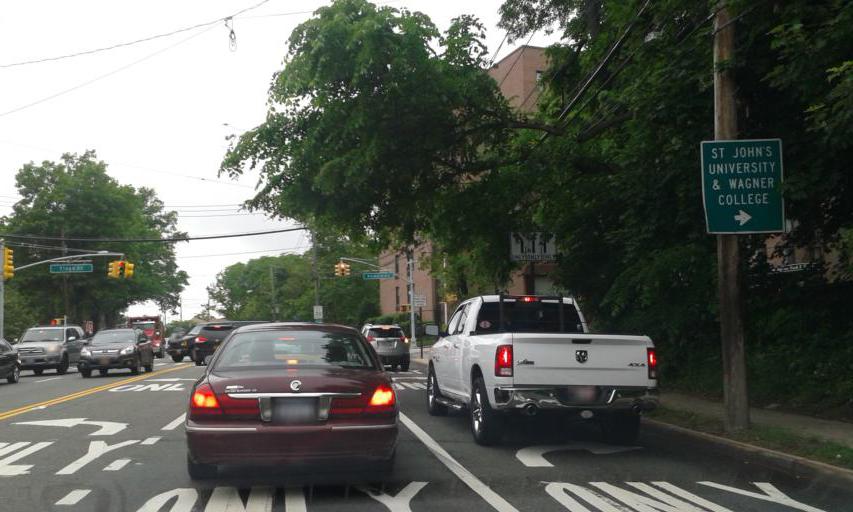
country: US
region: New Jersey
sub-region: Hudson County
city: Bayonne
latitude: 40.6120
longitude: -74.0988
